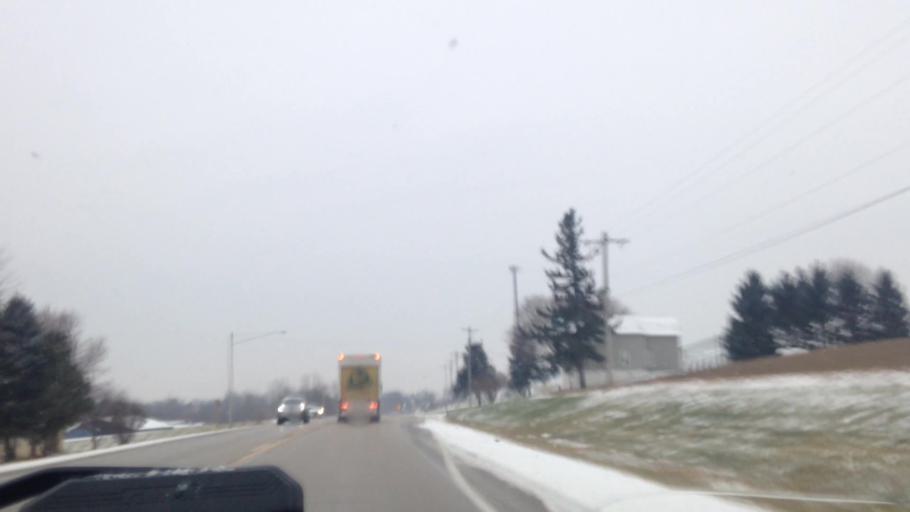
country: US
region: Wisconsin
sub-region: Dodge County
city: Hustisford
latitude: 43.4006
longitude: -88.5419
